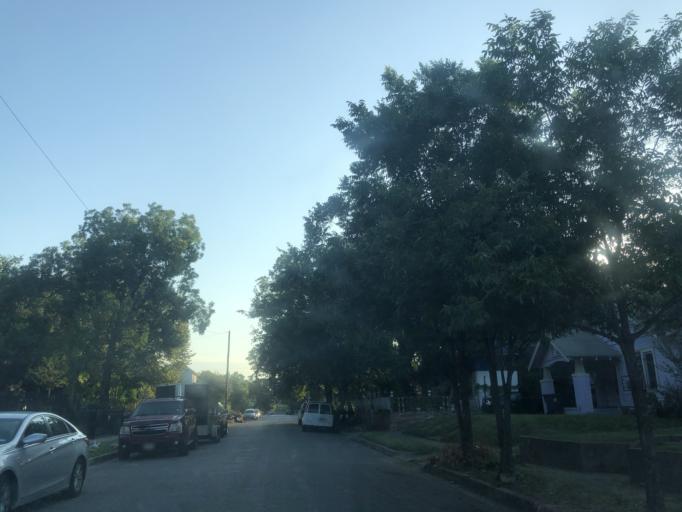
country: US
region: Texas
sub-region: Dallas County
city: Dallas
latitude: 32.7507
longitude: -96.7666
